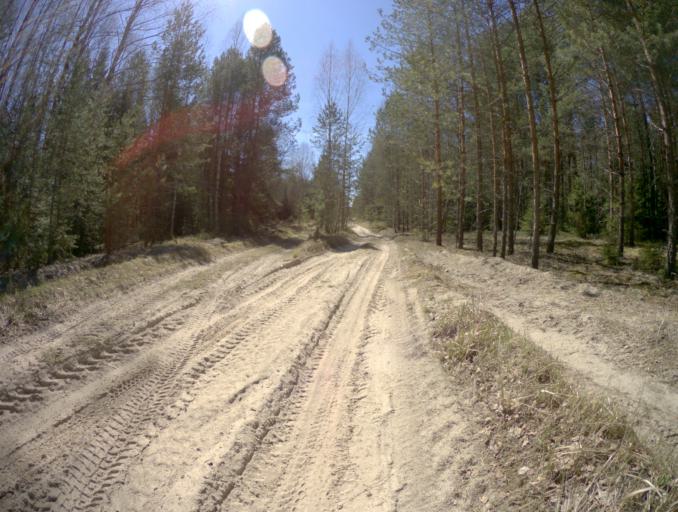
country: RU
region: Vladimir
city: Golovino
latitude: 55.8847
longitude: 40.4062
